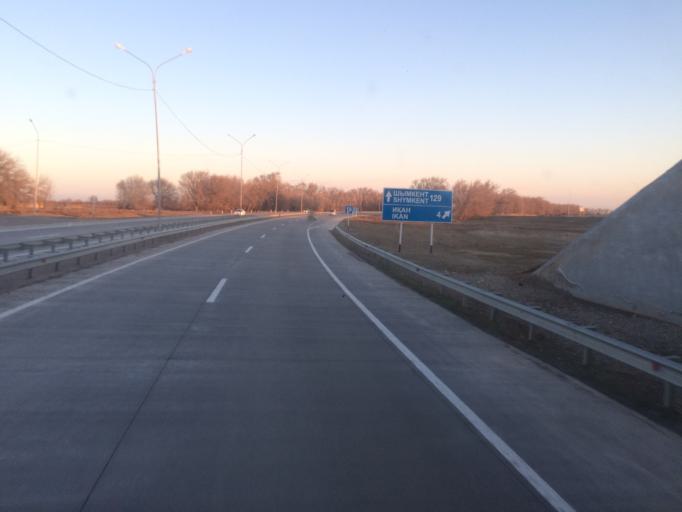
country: KZ
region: Ongtustik Qazaqstan
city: Turkestan
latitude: 43.1546
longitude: 68.5677
